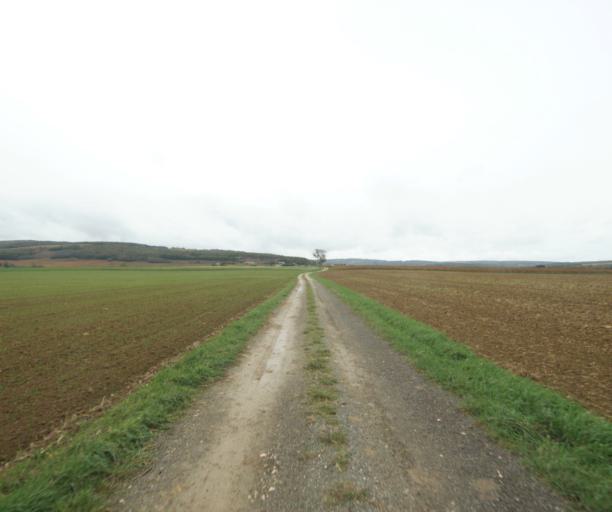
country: FR
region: Rhone-Alpes
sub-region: Departement de l'Ain
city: Pont-de-Vaux
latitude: 46.4678
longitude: 4.8672
